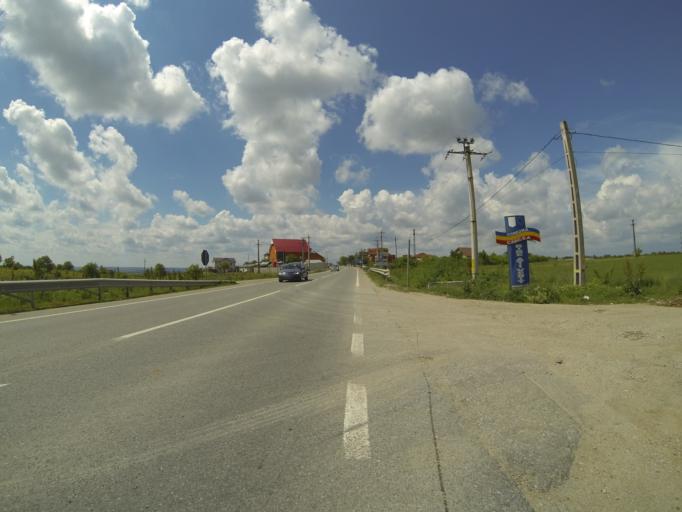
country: RO
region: Dolj
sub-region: Comuna Carcea
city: Carcea
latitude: 44.2627
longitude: 23.9030
